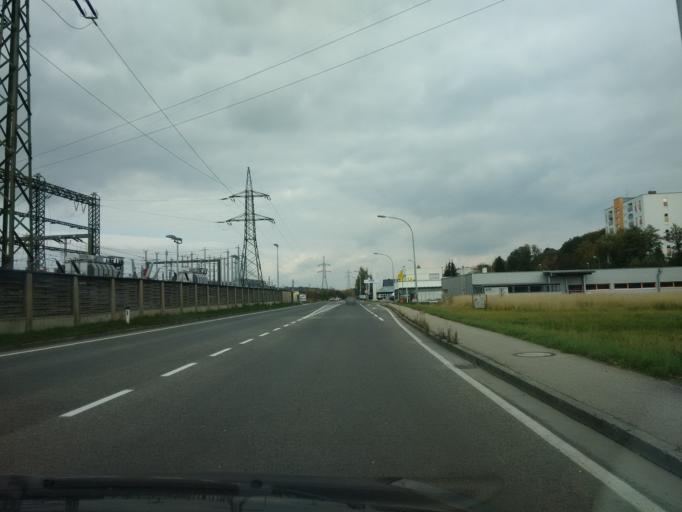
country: AT
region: Upper Austria
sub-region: Politischer Bezirk Vocklabruck
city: Redlham
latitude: 48.0185
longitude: 13.7274
